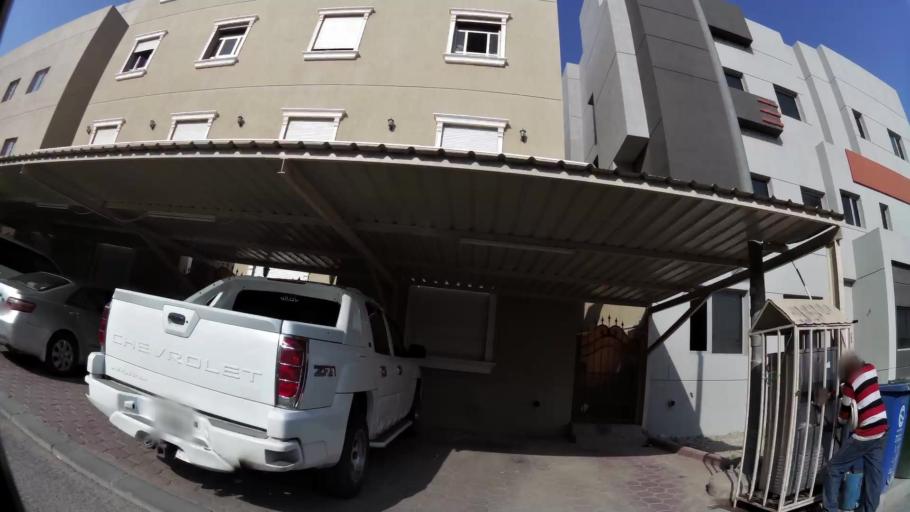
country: KW
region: Al Asimah
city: Ar Rabiyah
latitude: 29.3006
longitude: 47.8092
